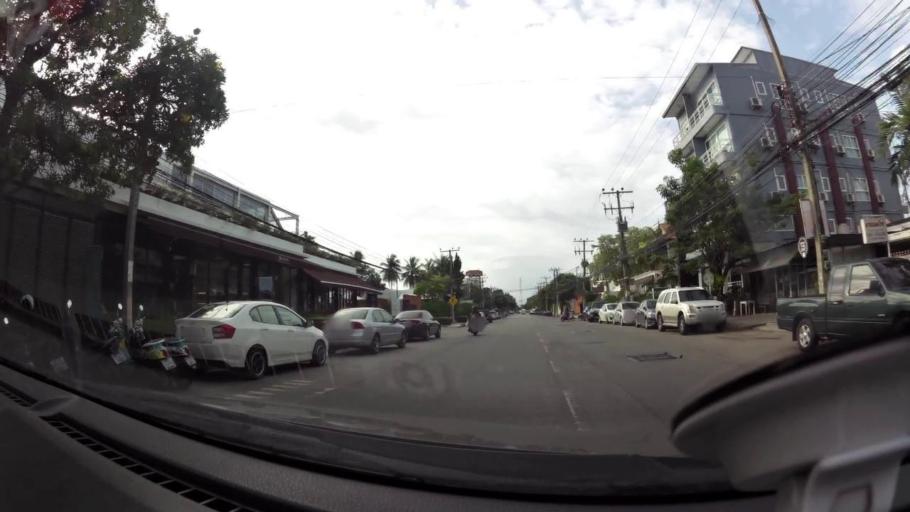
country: TH
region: Prachuap Khiri Khan
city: Hua Hin
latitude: 12.5766
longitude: 99.9565
